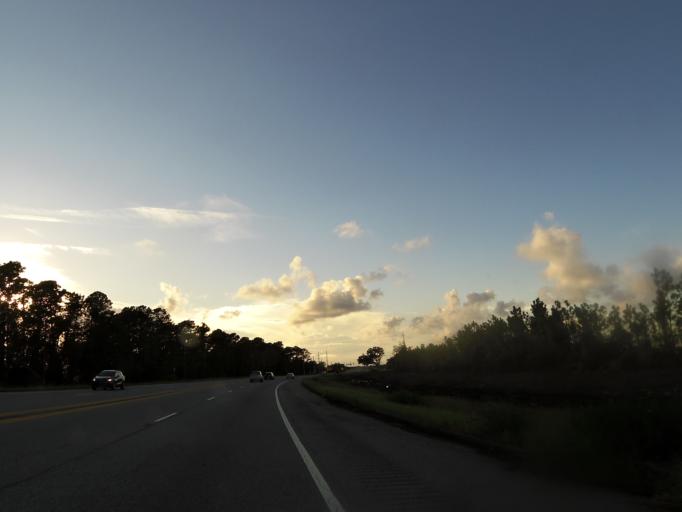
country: US
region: Georgia
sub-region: Glynn County
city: Brunswick
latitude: 31.1149
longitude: -81.5355
